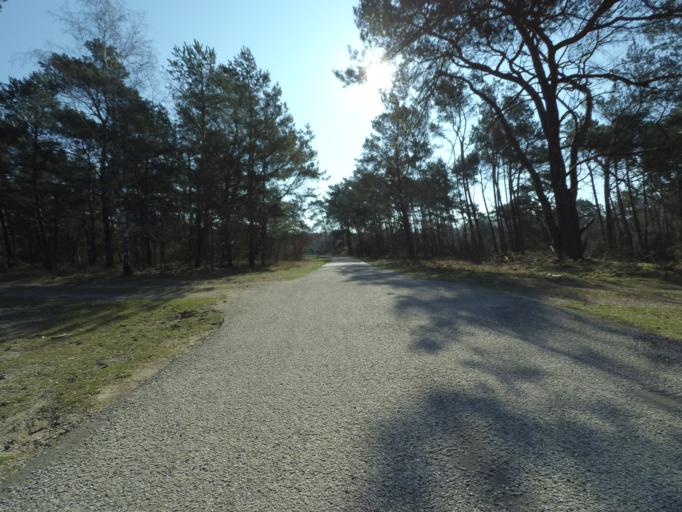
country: NL
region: Gelderland
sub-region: Gemeente Ede
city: Otterlo
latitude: 52.0985
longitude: 5.8128
